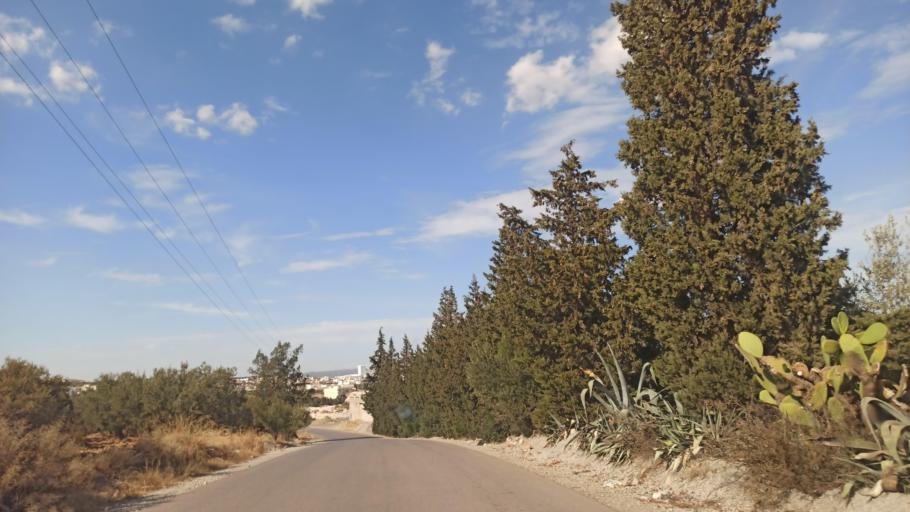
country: TN
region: Zaghwan
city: Zaghouan
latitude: 36.3396
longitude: 10.2094
